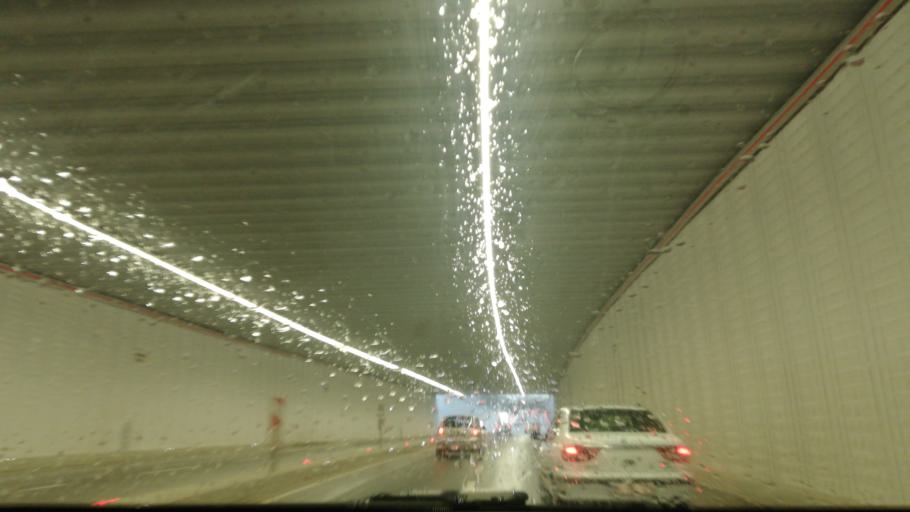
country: TR
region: Kahramanmaras
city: Kahramanmaras
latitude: 37.5846
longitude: 36.9048
